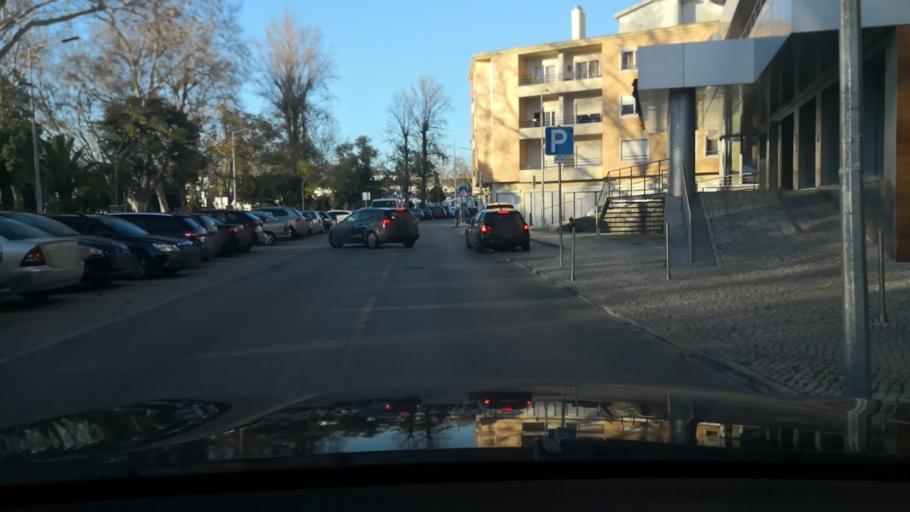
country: PT
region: Setubal
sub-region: Setubal
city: Setubal
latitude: 38.5285
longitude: -8.8900
